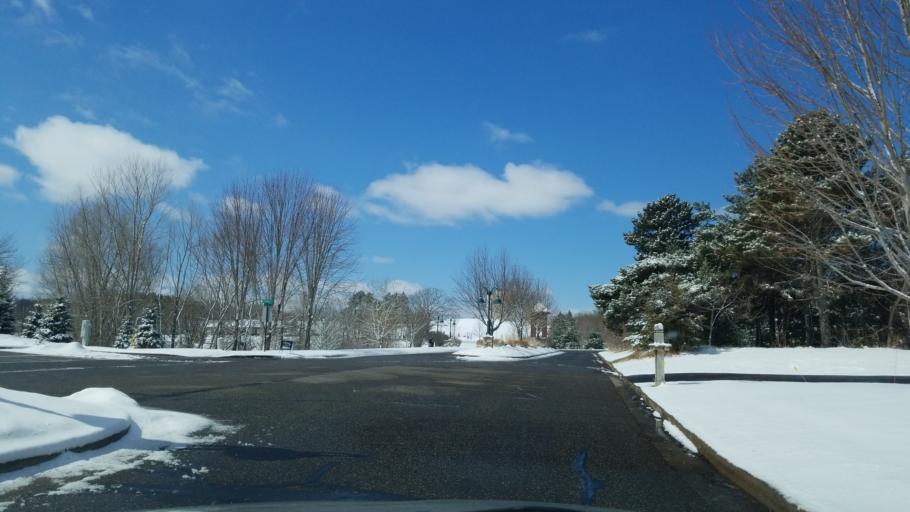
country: US
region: Wisconsin
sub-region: Saint Croix County
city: Hudson
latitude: 44.9551
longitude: -92.7093
